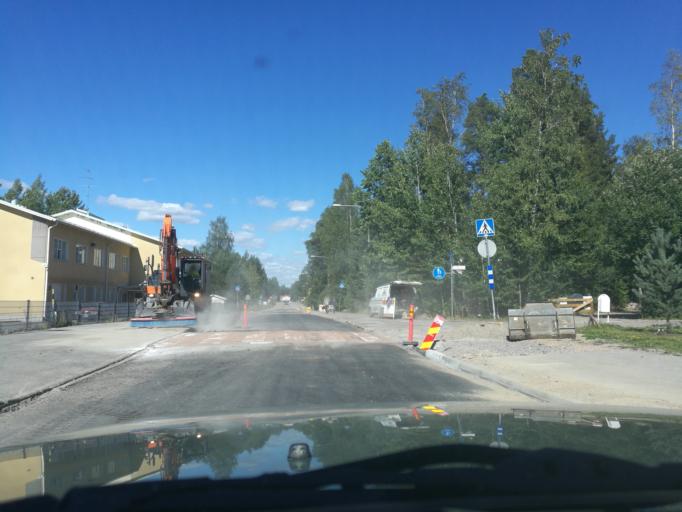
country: FI
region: Uusimaa
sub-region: Helsinki
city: Kerava
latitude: 60.3461
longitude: 25.1133
